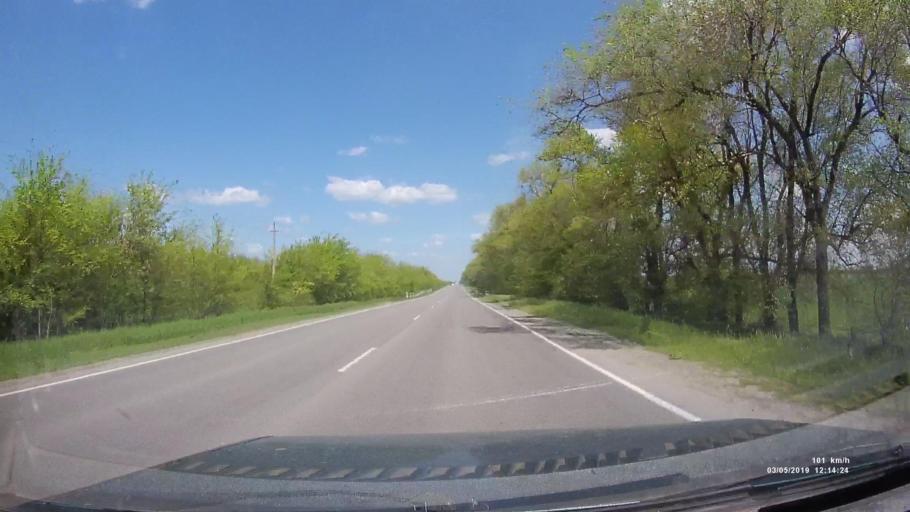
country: RU
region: Rostov
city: Melikhovskaya
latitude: 47.3435
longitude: 40.5631
